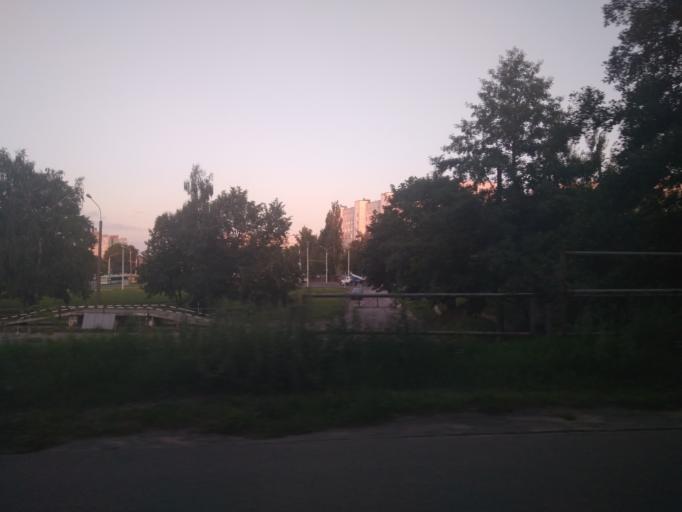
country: BY
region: Minsk
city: Novoye Medvezhino
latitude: 53.9249
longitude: 27.4745
